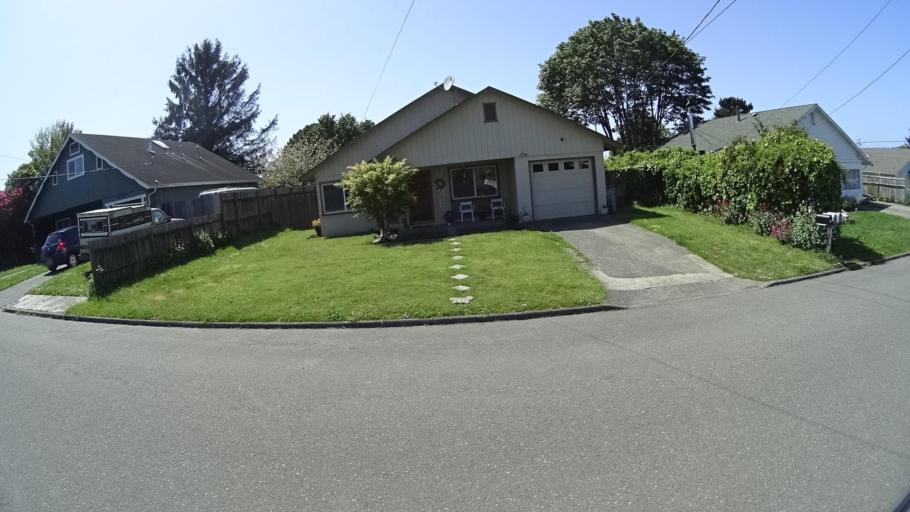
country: US
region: California
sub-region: Humboldt County
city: Fortuna
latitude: 40.5660
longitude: -124.1339
